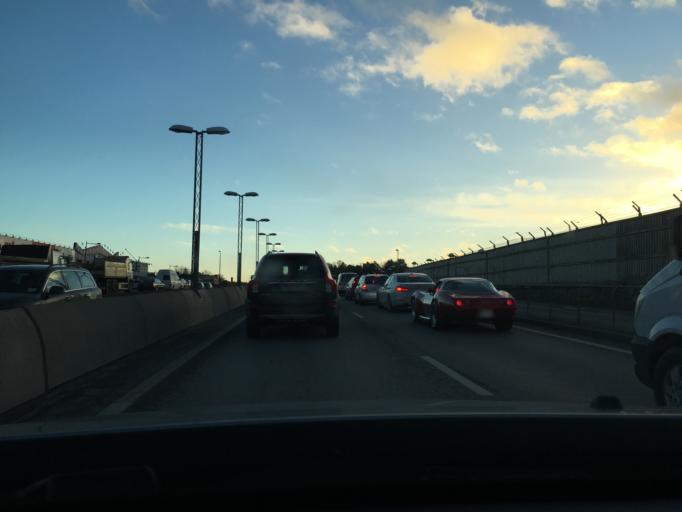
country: SE
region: Stockholm
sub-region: Sundbybergs Kommun
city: Sundbyberg
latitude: 59.3496
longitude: 17.9566
